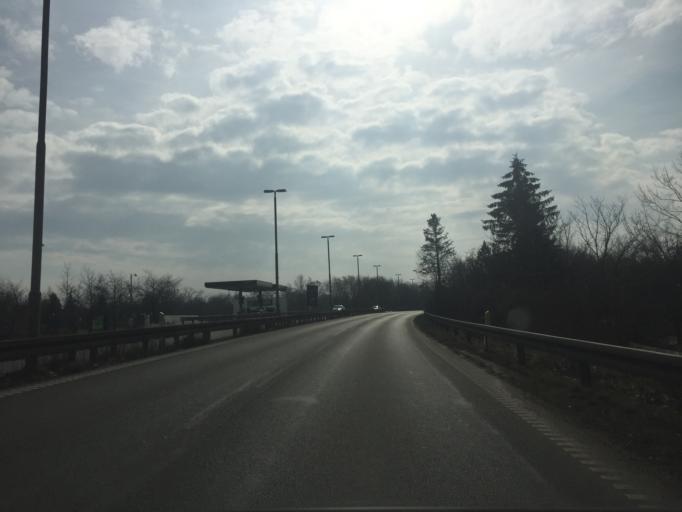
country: DK
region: Capital Region
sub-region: Lyngby-Tarbaek Kommune
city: Kongens Lyngby
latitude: 55.7895
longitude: 12.4866
